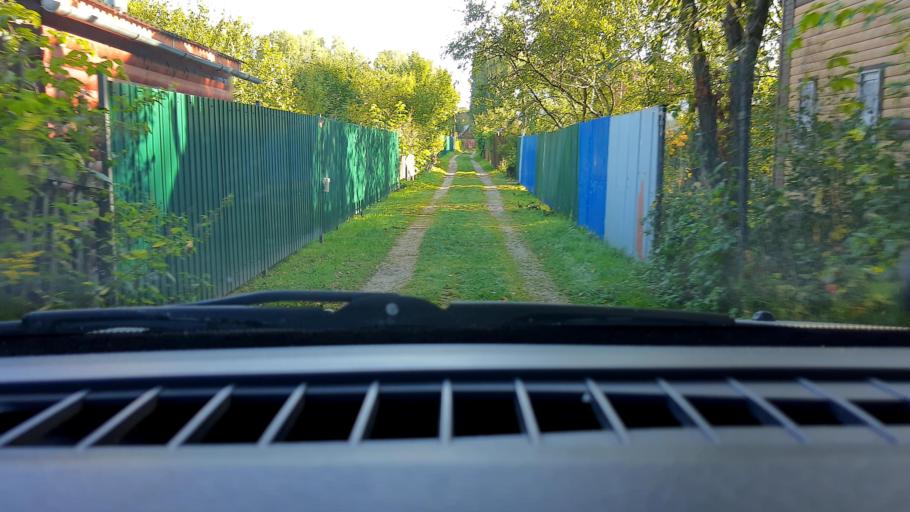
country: RU
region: Nizjnij Novgorod
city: Sitniki
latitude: 56.4676
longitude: 44.0342
